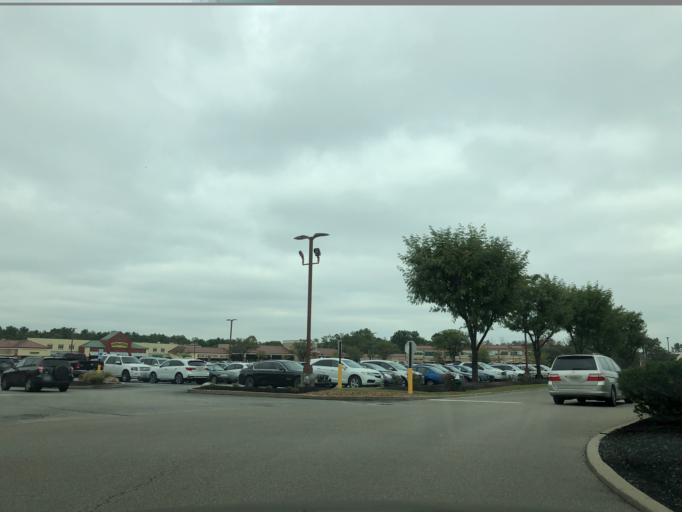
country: US
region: Ohio
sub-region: Hamilton County
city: Sixteen Mile Stand
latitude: 39.2708
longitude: -84.3296
